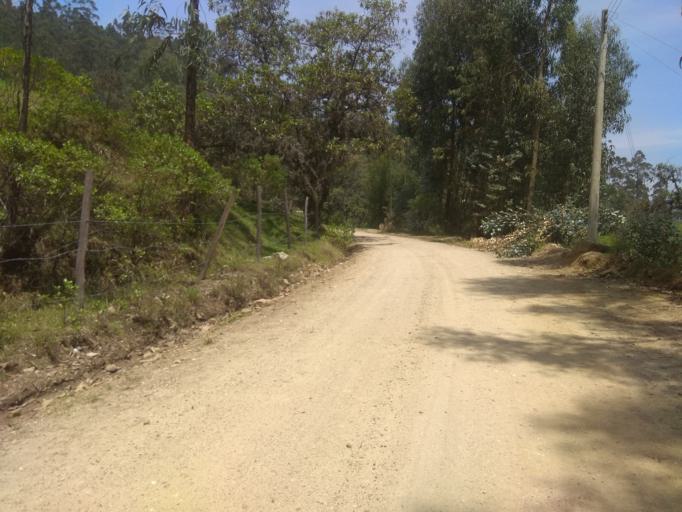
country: CO
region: Boyaca
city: Socha Viejo
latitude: 5.9797
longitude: -72.7304
